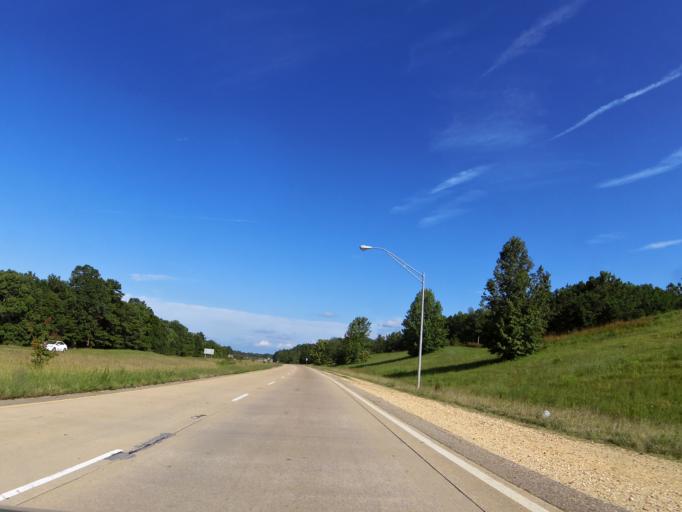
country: US
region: Mississippi
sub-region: Tishomingo County
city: Iuka
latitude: 34.7906
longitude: -88.2034
